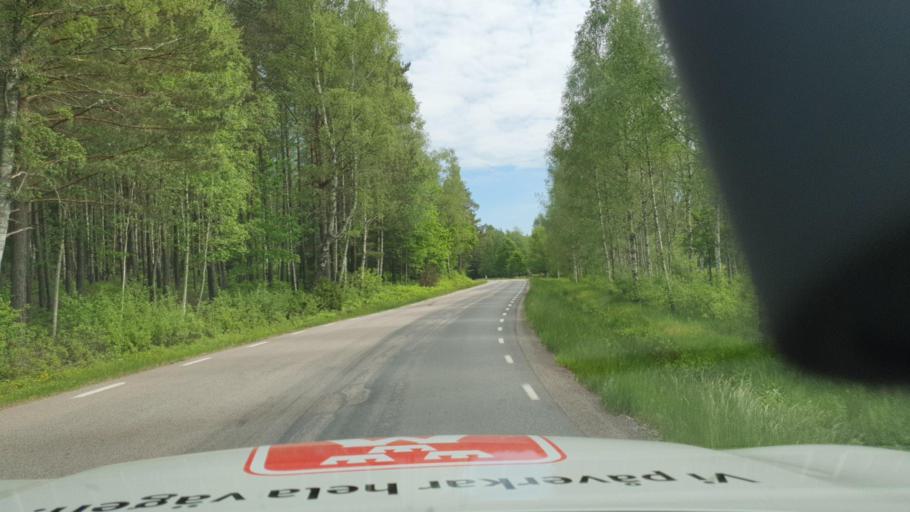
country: SE
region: Vaestra Goetaland
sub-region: Alingsas Kommun
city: Sollebrunn
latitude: 58.2108
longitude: 12.5486
